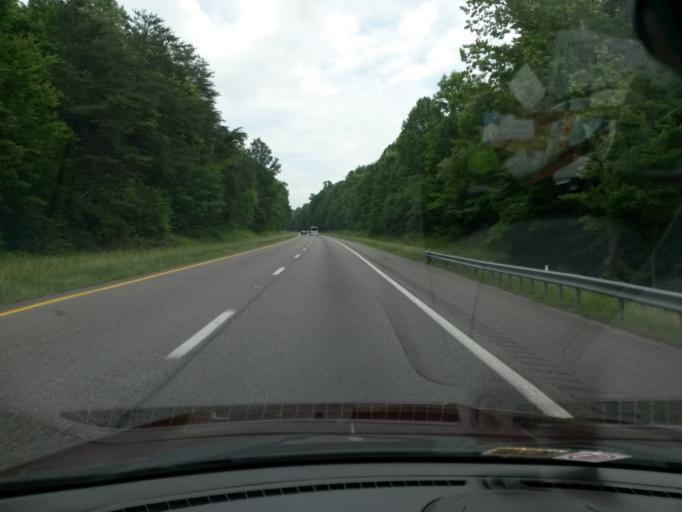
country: US
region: Virginia
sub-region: Goochland County
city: Goochland
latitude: 37.7185
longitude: -77.8103
